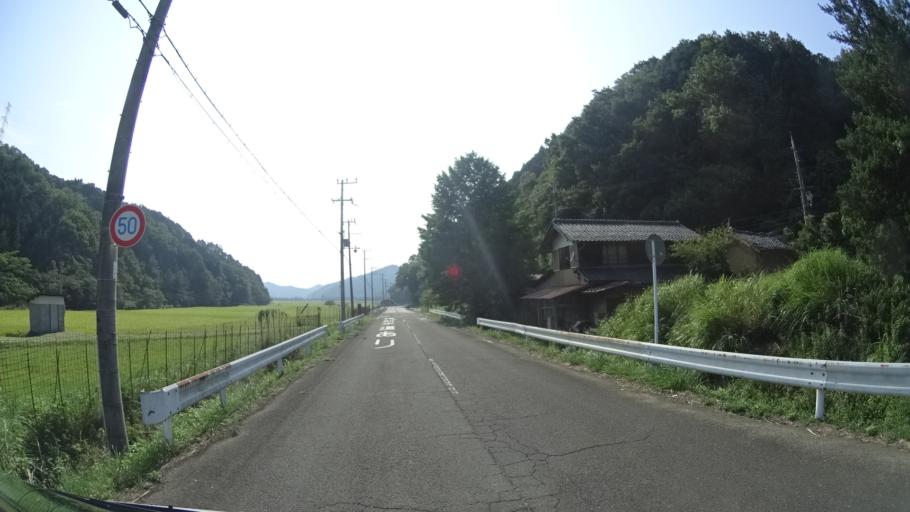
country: JP
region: Kyoto
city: Maizuru
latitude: 35.4336
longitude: 135.2686
